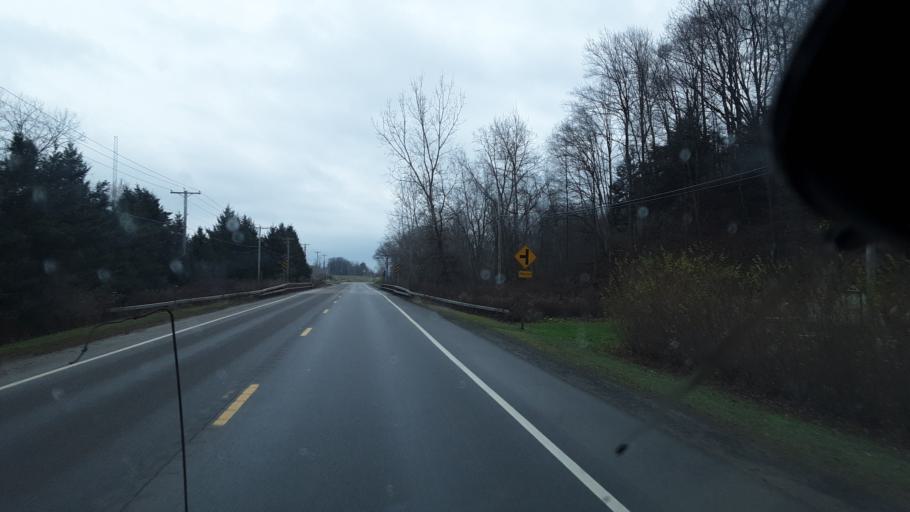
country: US
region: New York
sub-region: Wyoming County
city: Arcade
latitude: 42.4881
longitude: -78.3699
